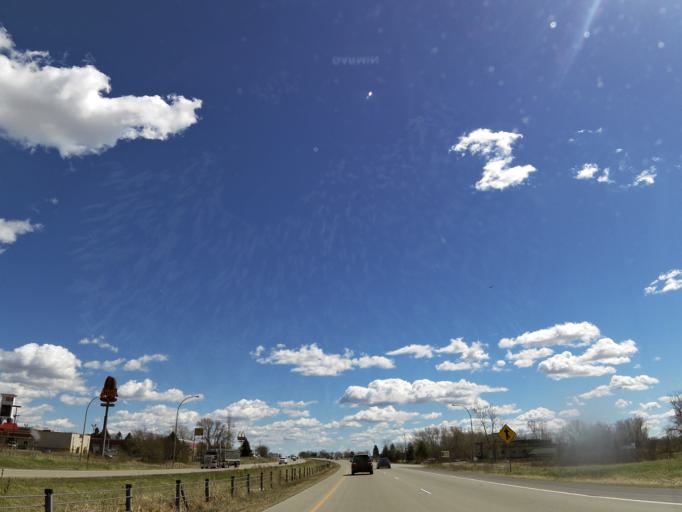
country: US
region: Minnesota
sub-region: Washington County
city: Cottage Grove
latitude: 44.8312
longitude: -92.9627
